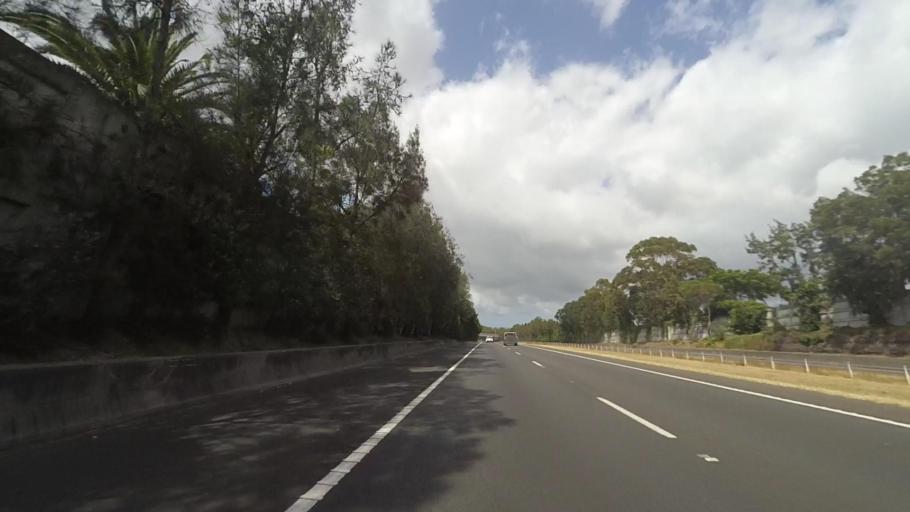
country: AU
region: New South Wales
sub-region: Wollongong
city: Dapto
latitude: -34.5006
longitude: 150.7950
